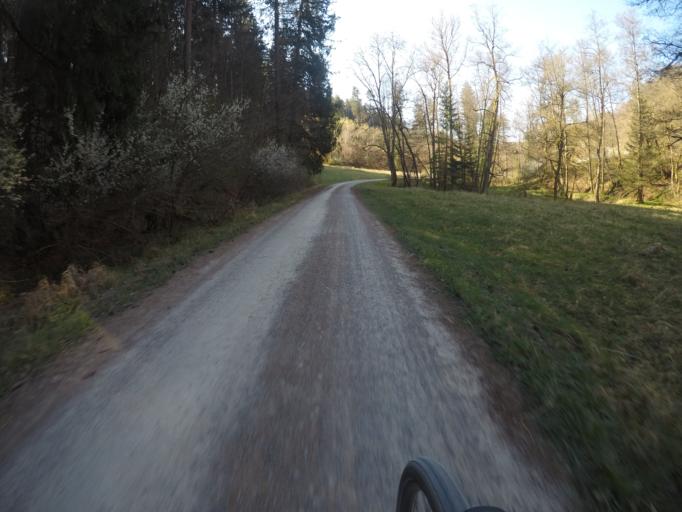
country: DE
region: Baden-Wuerttemberg
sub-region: Regierungsbezirk Stuttgart
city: Weil im Schonbuch
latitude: 48.5810
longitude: 9.0377
